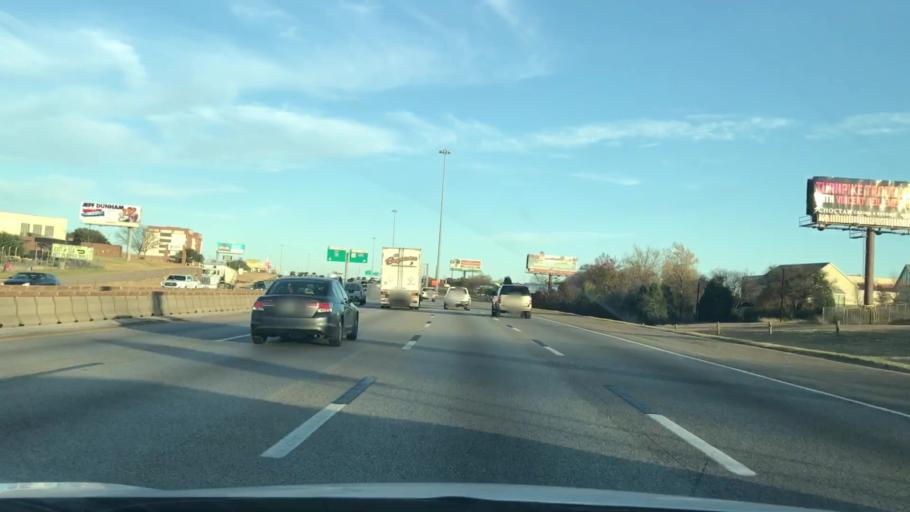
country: US
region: Texas
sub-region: Dallas County
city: Highland Park
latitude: 32.7940
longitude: -96.7098
